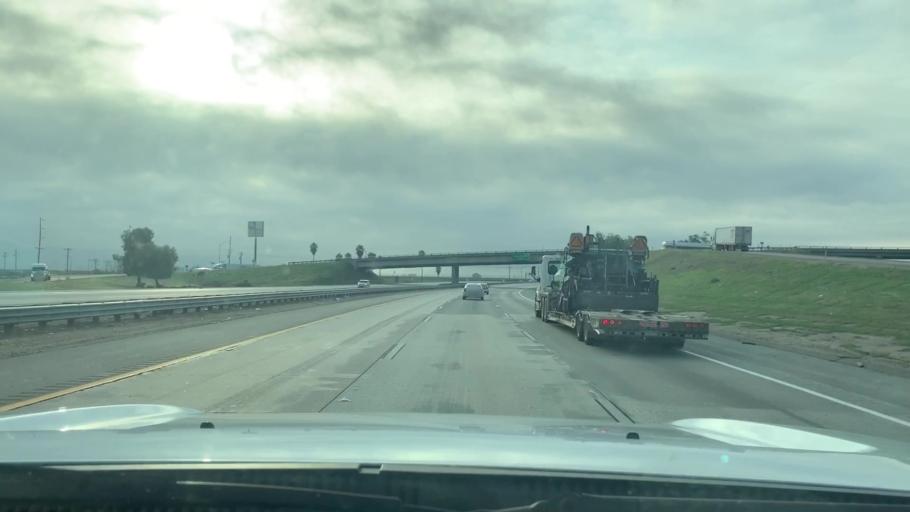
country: US
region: California
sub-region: Kern County
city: Shafter
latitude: 35.5315
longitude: -119.1908
